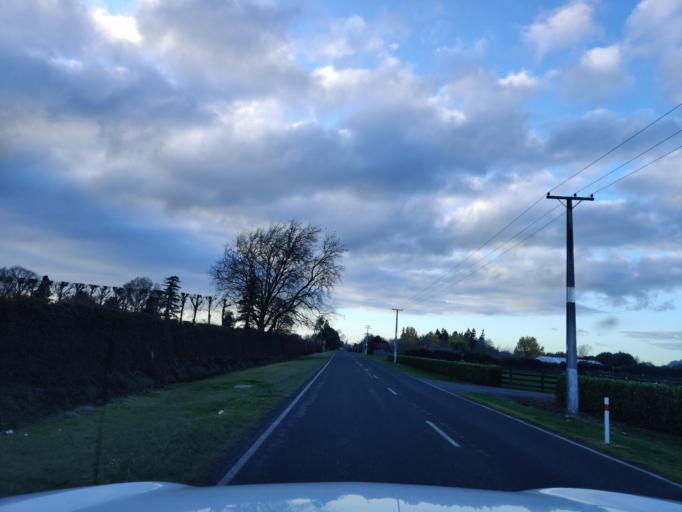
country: NZ
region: Waikato
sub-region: Waipa District
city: Cambridge
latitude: -37.8565
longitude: 175.4390
